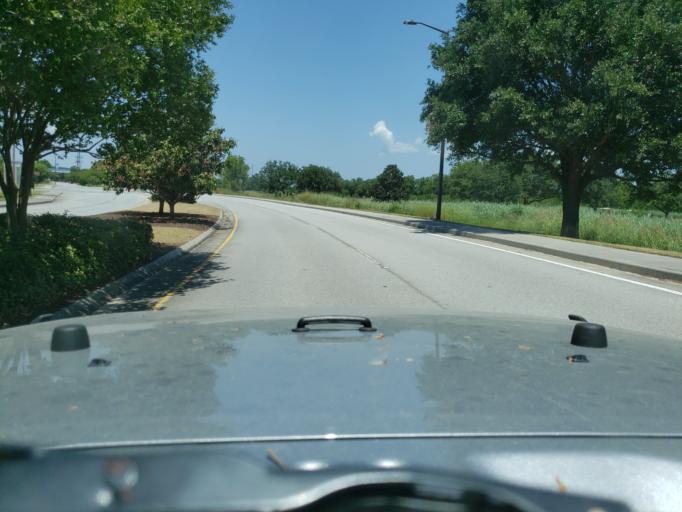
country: US
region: Georgia
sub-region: Chatham County
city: Savannah
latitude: 32.0876
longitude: -81.0854
